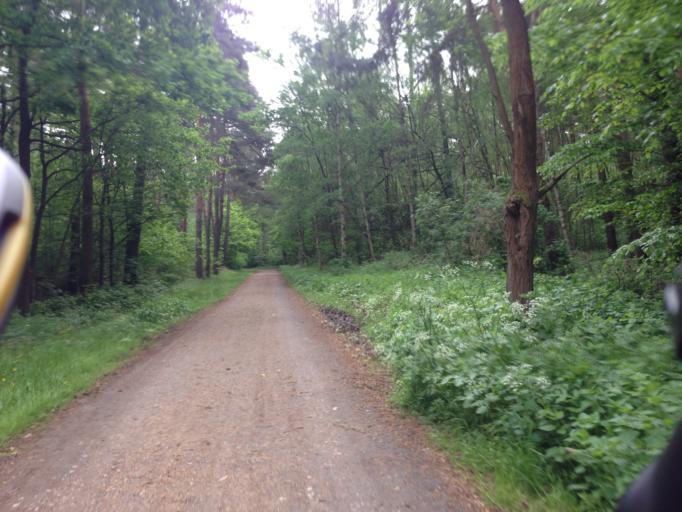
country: DE
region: Hesse
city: Obertshausen
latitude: 50.0788
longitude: 8.8818
